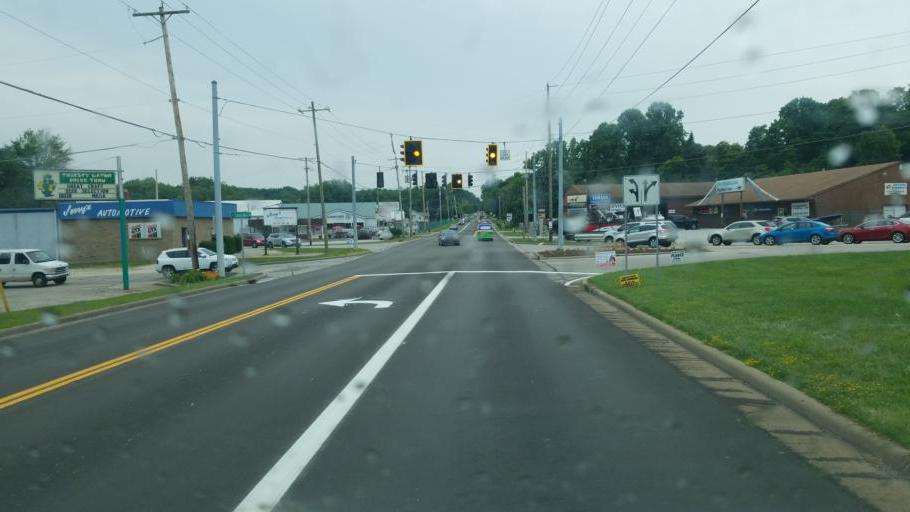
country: US
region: Ohio
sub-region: Summit County
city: Portage Lakes
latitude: 40.9984
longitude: -81.5572
